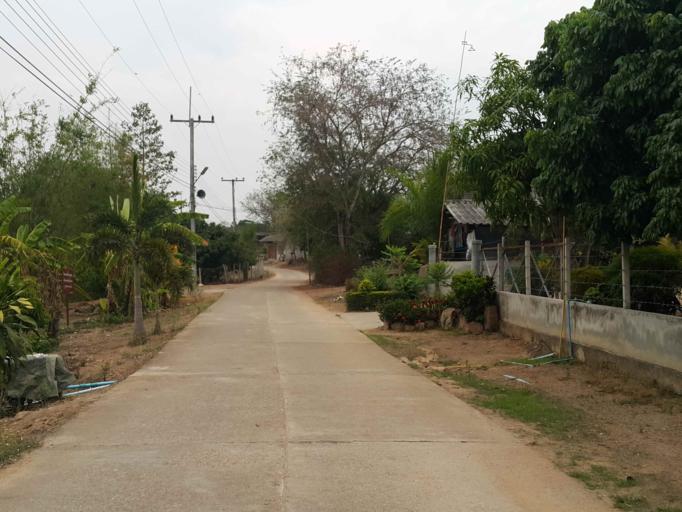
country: TH
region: Chiang Mai
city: Mae Taeng
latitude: 19.1037
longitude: 98.9981
